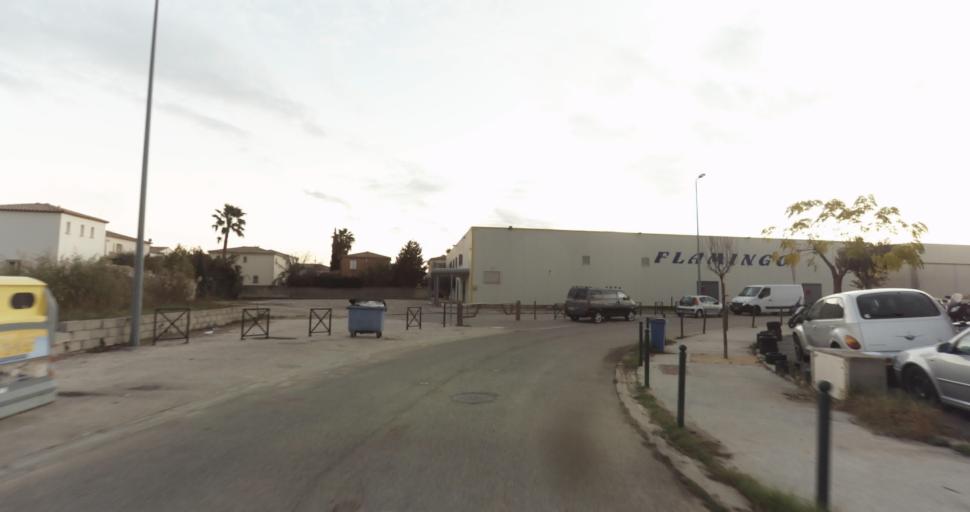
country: FR
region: Languedoc-Roussillon
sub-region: Departement du Gard
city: Aigues-Mortes
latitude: 43.5772
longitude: 4.1903
